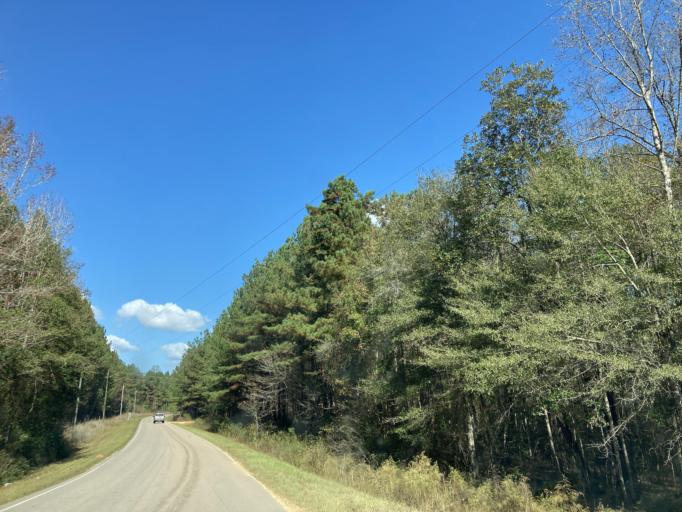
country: US
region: Mississippi
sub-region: Lamar County
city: Sumrall
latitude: 31.3138
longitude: -89.5422
